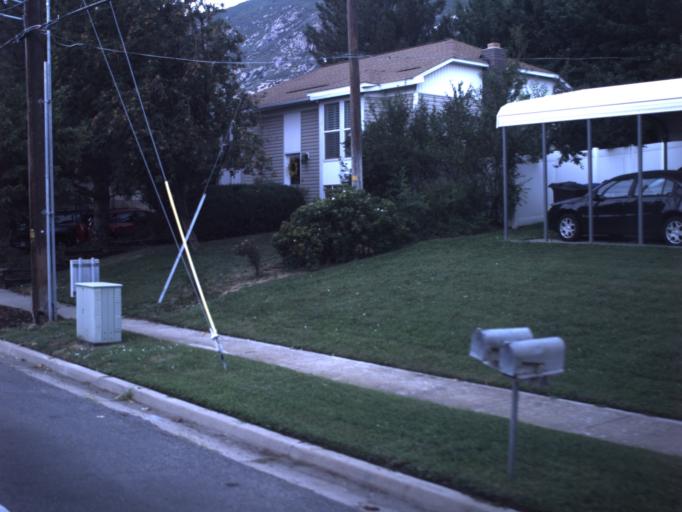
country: US
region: Utah
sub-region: Davis County
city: Farmington
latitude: 40.9675
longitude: -111.8834
